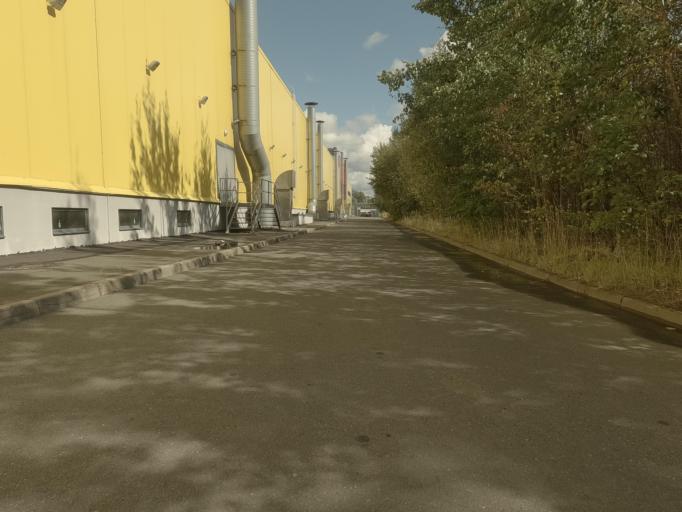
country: RU
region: St.-Petersburg
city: Krasnogvargeisky
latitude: 59.9299
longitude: 30.4318
